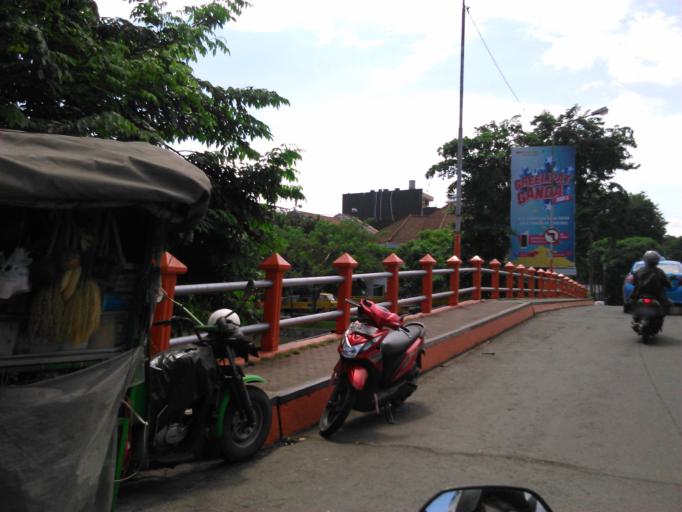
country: ID
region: East Java
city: Gubengairlangga
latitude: -7.2773
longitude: 112.7438
